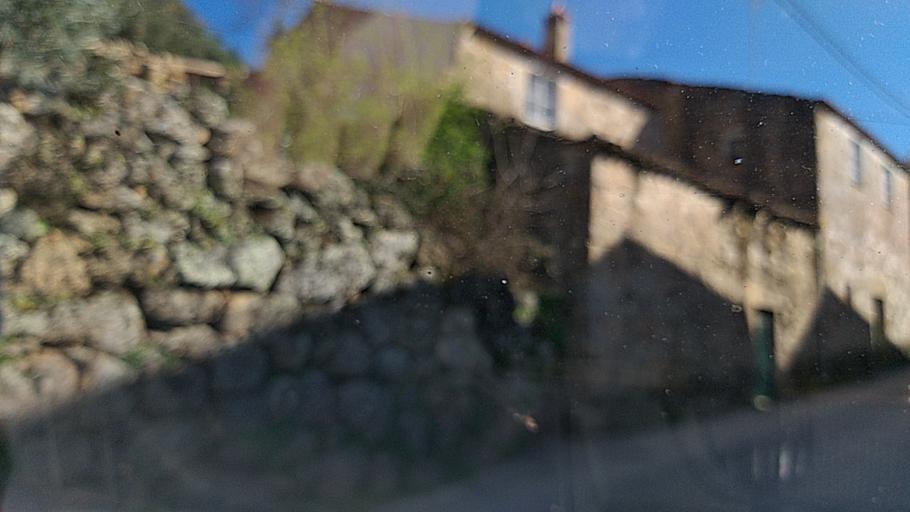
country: PT
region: Guarda
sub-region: Guarda
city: Guarda
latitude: 40.5892
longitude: -7.2884
